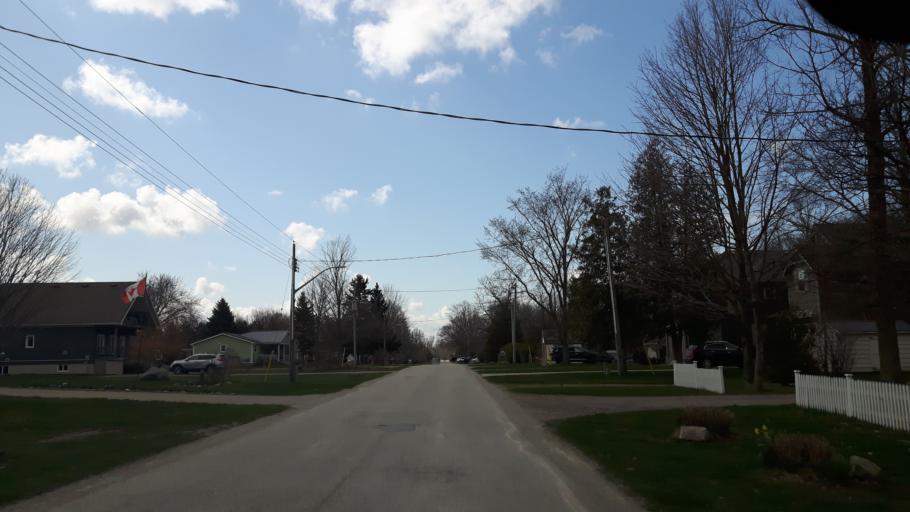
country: CA
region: Ontario
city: Bluewater
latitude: 43.5563
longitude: -81.7049
